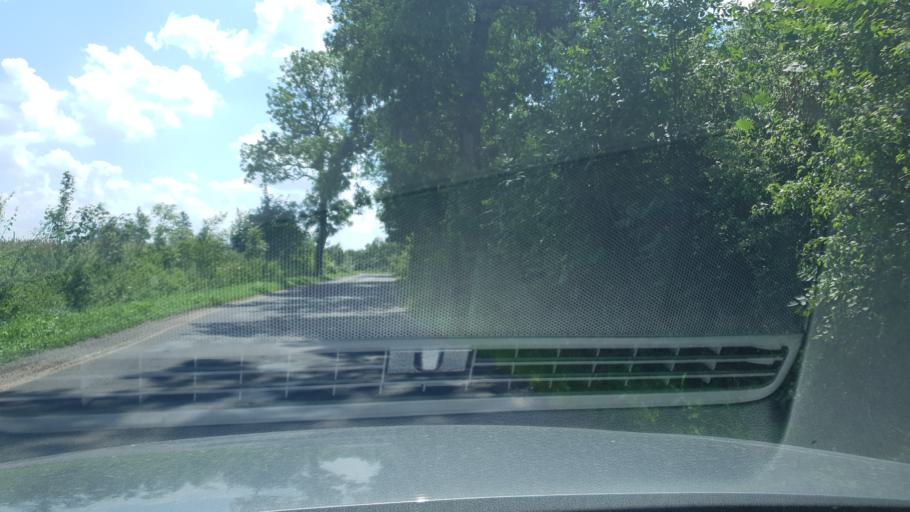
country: PL
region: Kujawsko-Pomorskie
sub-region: Powiat wabrzeski
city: Pluznica
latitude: 53.3536
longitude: 18.8237
